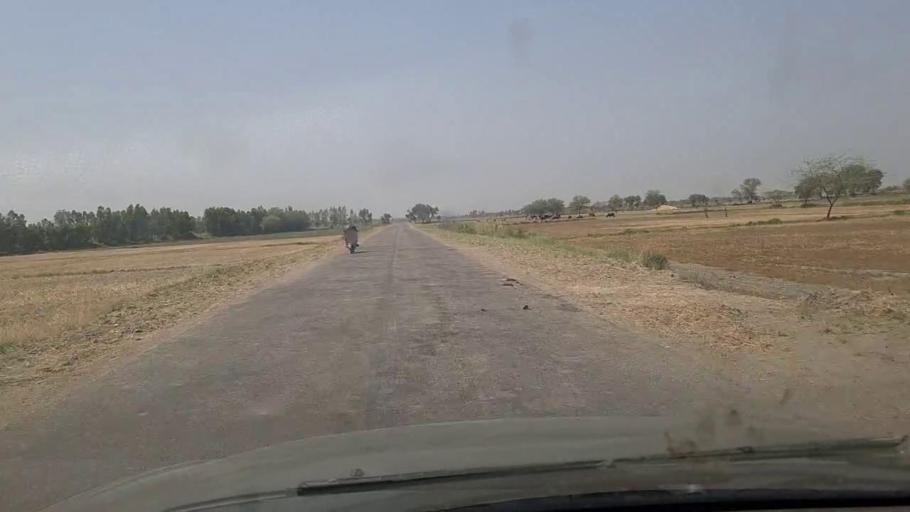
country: PK
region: Sindh
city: Khanpur
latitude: 27.8649
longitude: 69.4422
